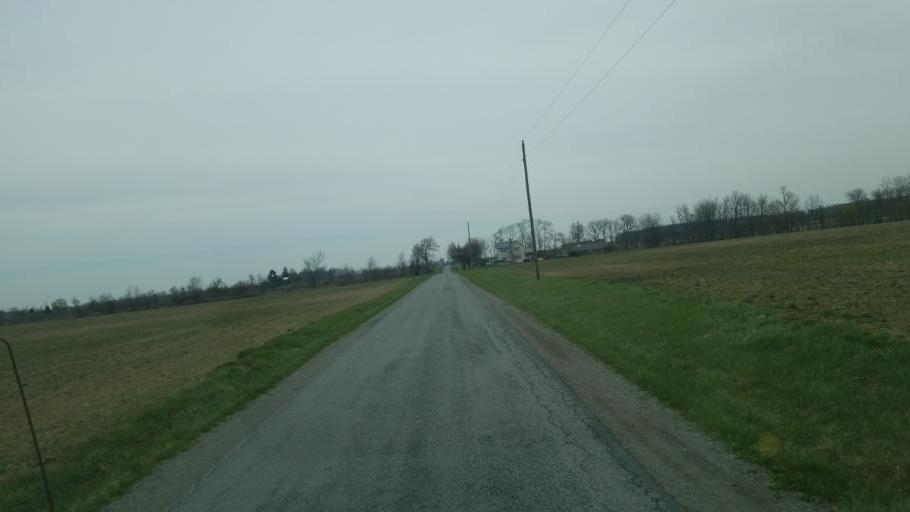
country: US
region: Ohio
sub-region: Hardin County
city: Forest
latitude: 40.8982
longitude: -83.5149
